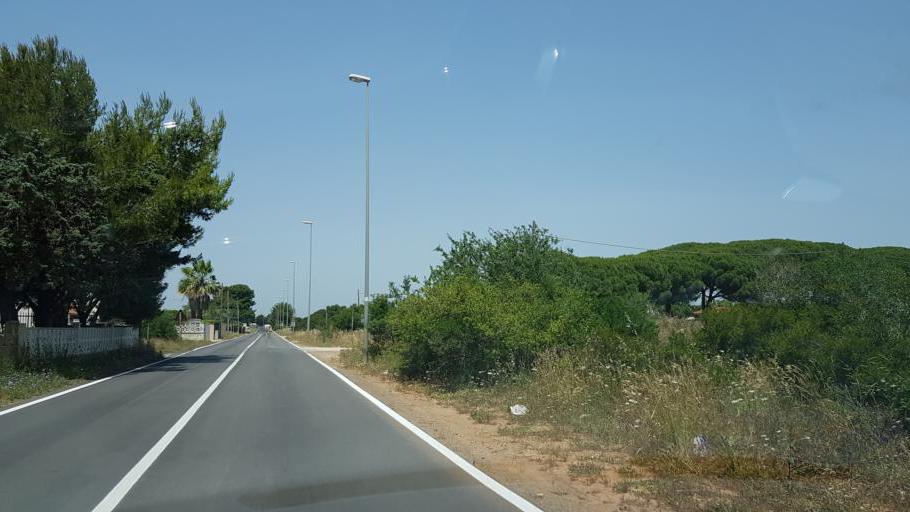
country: IT
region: Apulia
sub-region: Provincia di Lecce
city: Porto Cesareo
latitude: 40.2462
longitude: 17.9132
